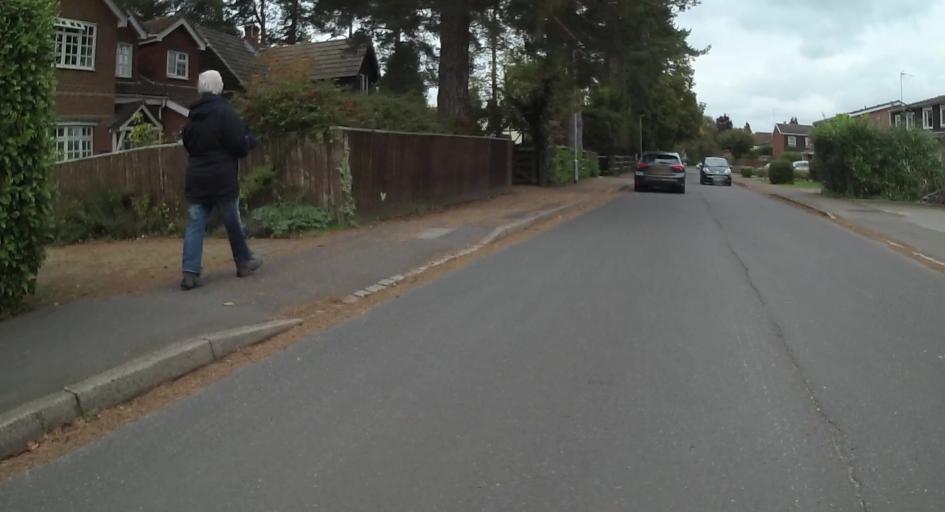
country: GB
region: England
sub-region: Wokingham
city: Finchampstead
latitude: 51.3807
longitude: -0.8602
